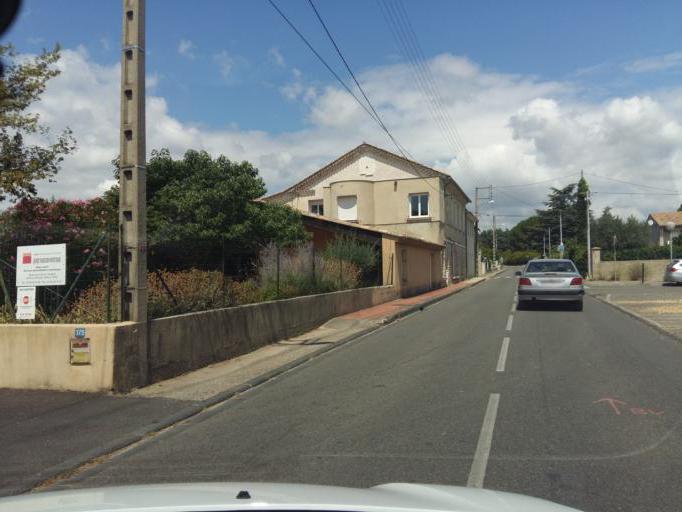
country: FR
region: Provence-Alpes-Cote d'Azur
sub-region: Departement du Vaucluse
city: Vaison-la-Romaine
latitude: 44.2476
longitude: 5.0682
